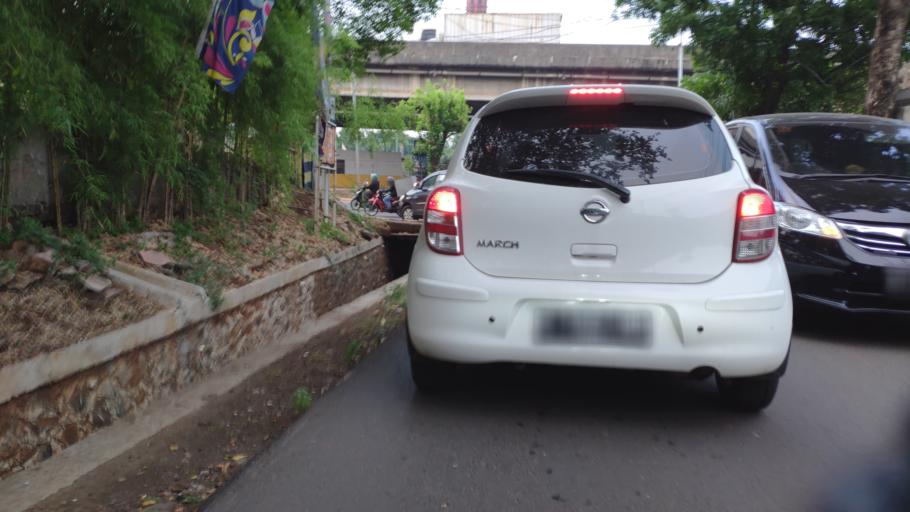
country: ID
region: West Java
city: Pamulang
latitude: -6.2928
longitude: 106.7987
